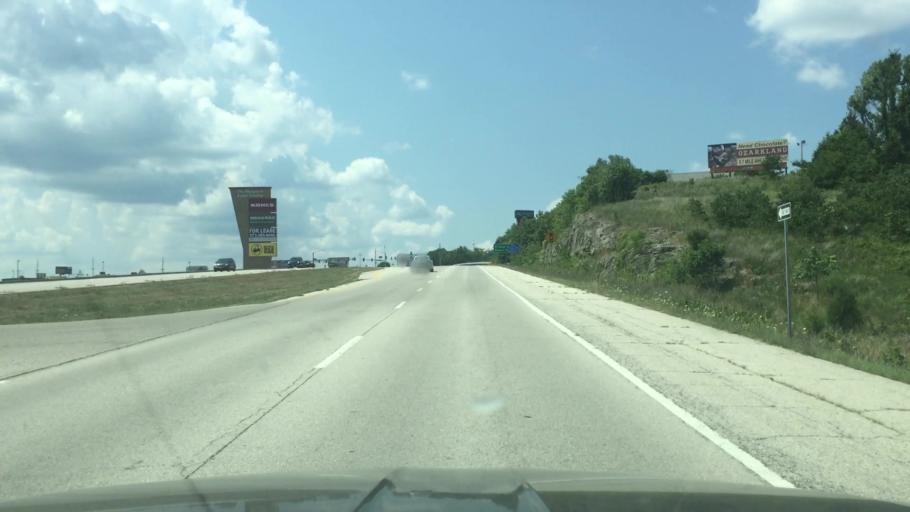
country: US
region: Missouri
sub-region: Miller County
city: Lake Ozark
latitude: 38.1786
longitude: -92.6136
